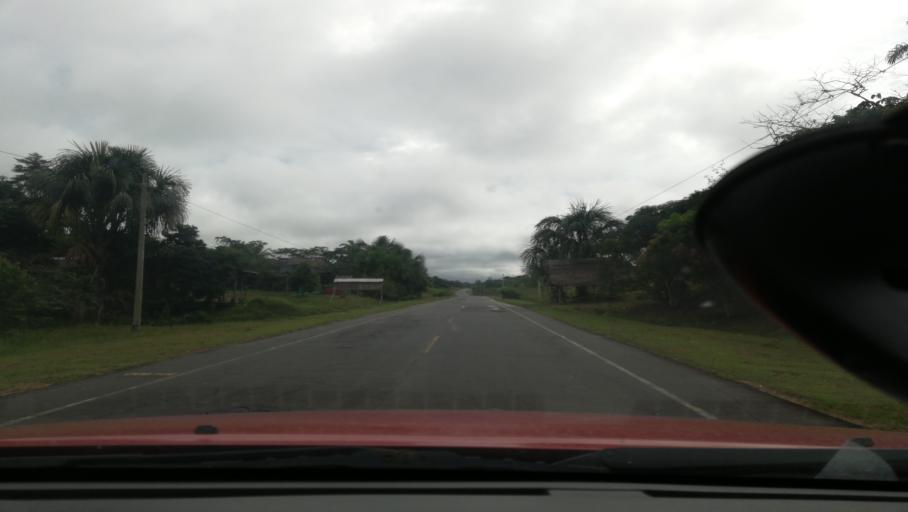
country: PE
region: Loreto
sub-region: Provincia de Loreto
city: Nauta
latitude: -4.3411
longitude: -73.5386
